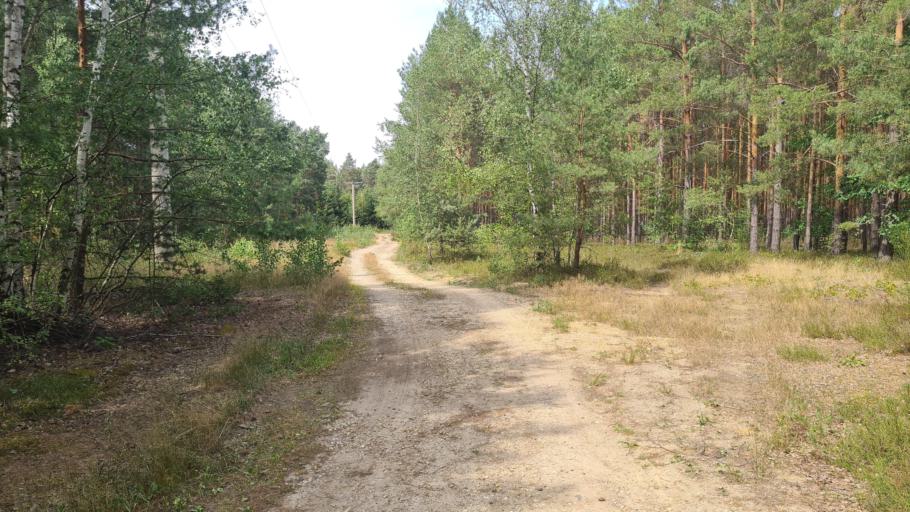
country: DE
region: Brandenburg
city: Sallgast
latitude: 51.5908
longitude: 13.9027
